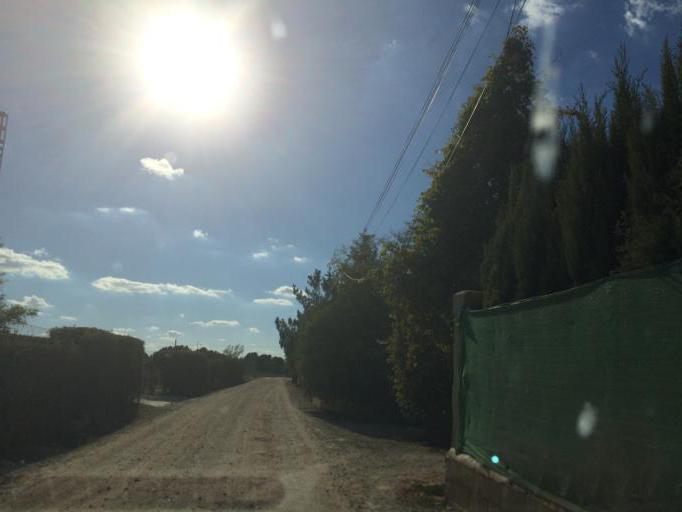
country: ES
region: Castille-La Mancha
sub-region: Provincia de Albacete
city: Albacete
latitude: 38.9928
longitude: -1.8881
